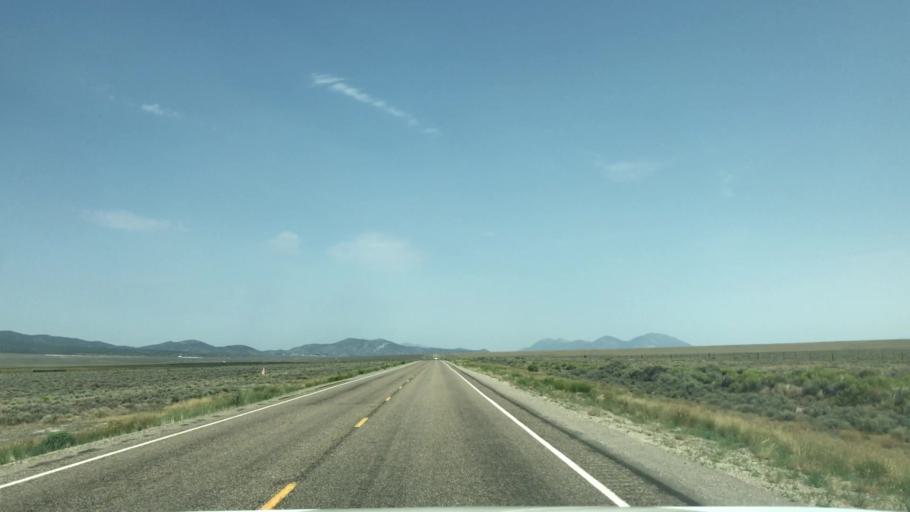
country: US
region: Nevada
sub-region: White Pine County
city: Ely
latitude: 39.1247
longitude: -114.7776
